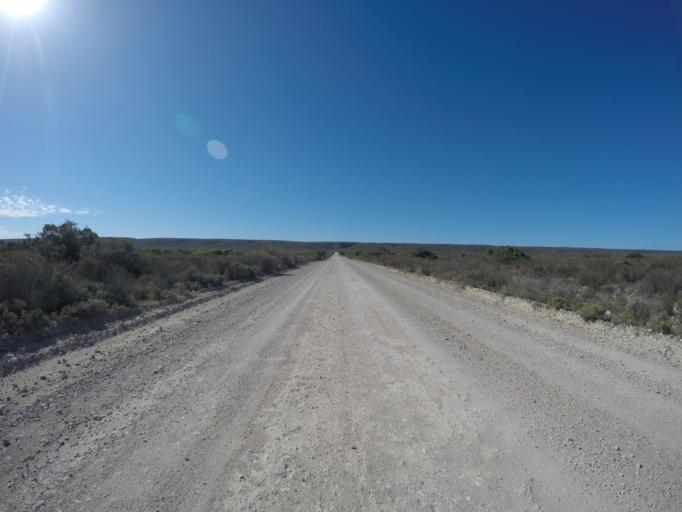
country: ZA
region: Western Cape
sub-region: Overberg District Municipality
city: Bredasdorp
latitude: -34.4444
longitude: 20.4218
